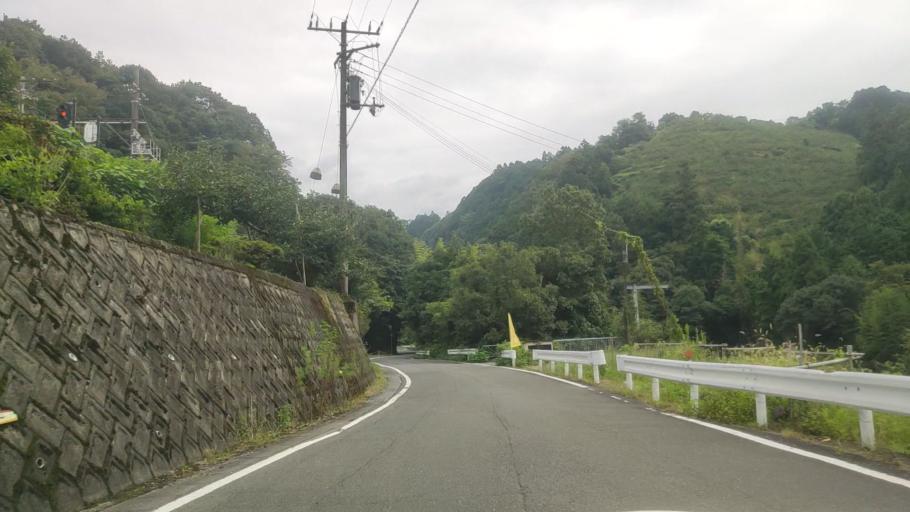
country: JP
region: Wakayama
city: Hashimoto
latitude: 34.2811
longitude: 135.5625
